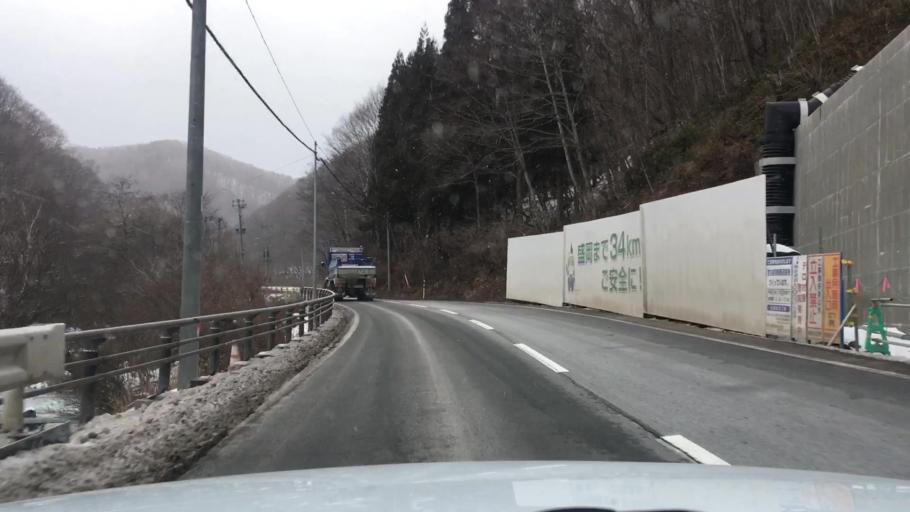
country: JP
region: Iwate
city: Tono
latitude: 39.6261
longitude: 141.4683
